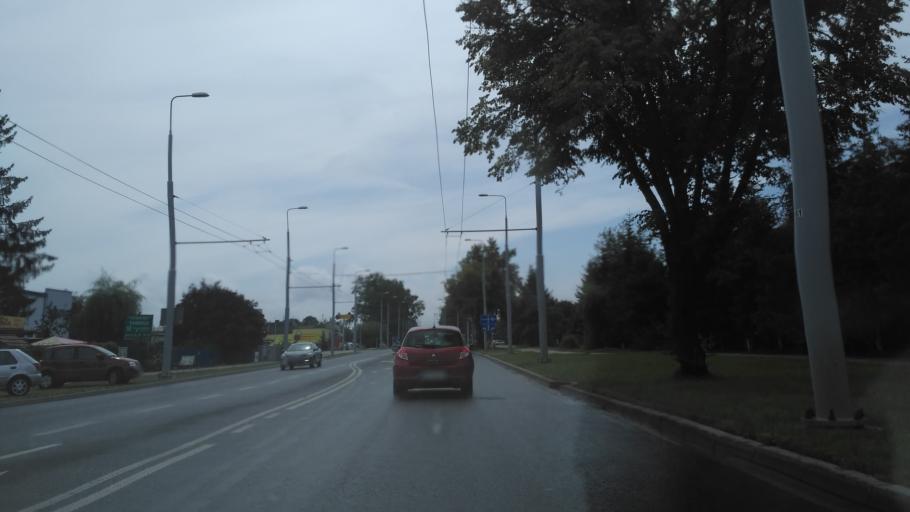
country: PL
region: Lublin Voivodeship
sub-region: Powiat lubelski
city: Lublin
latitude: 51.2024
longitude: 22.5859
